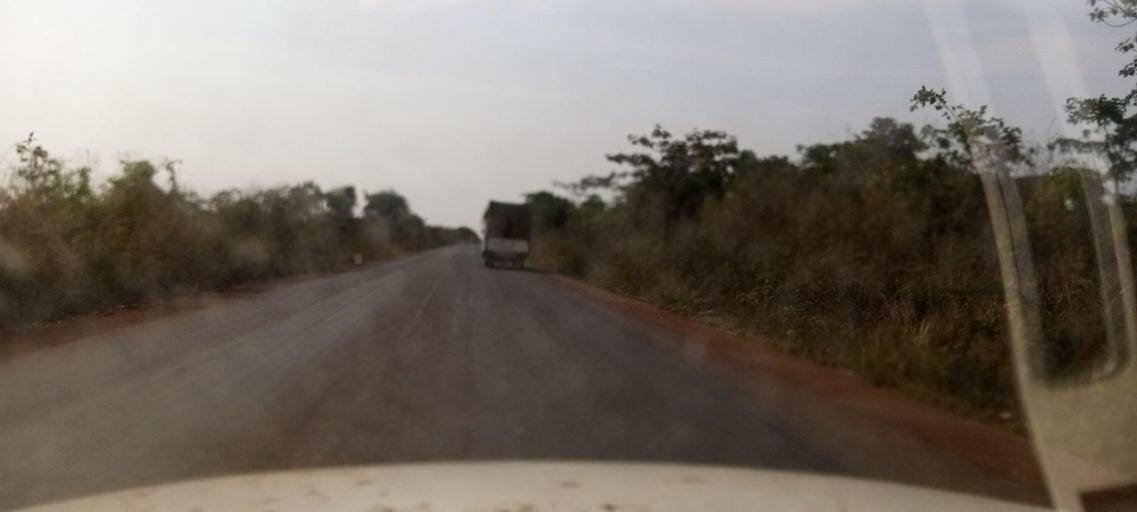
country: CD
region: Katanga
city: Lubumbashi
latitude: -11.3653
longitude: 27.3270
